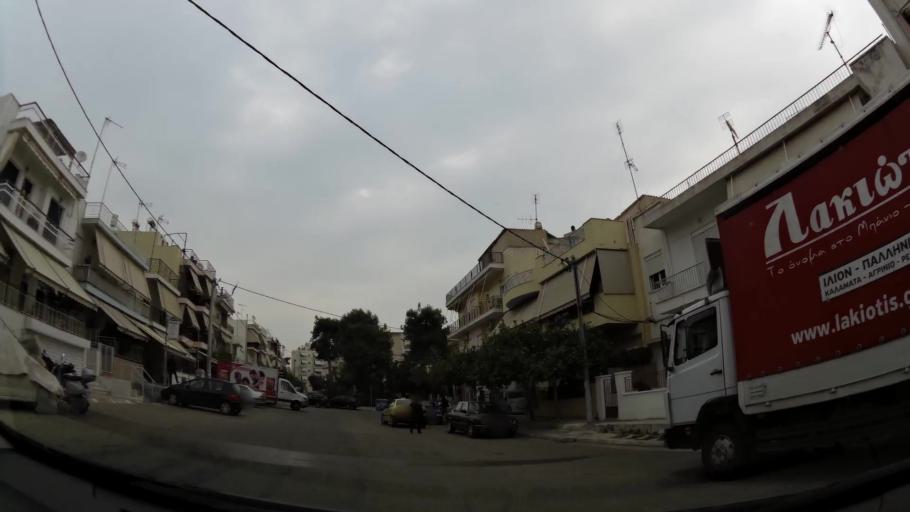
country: GR
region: Attica
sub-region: Nomos Piraios
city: Keratsini
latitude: 37.9771
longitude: 23.6252
